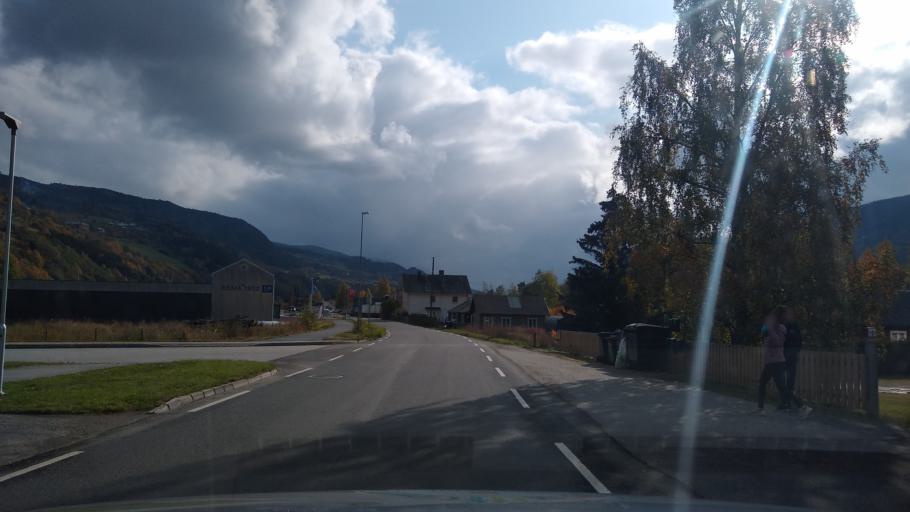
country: NO
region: Oppland
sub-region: Ringebu
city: Ringebu
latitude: 61.5312
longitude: 10.1432
